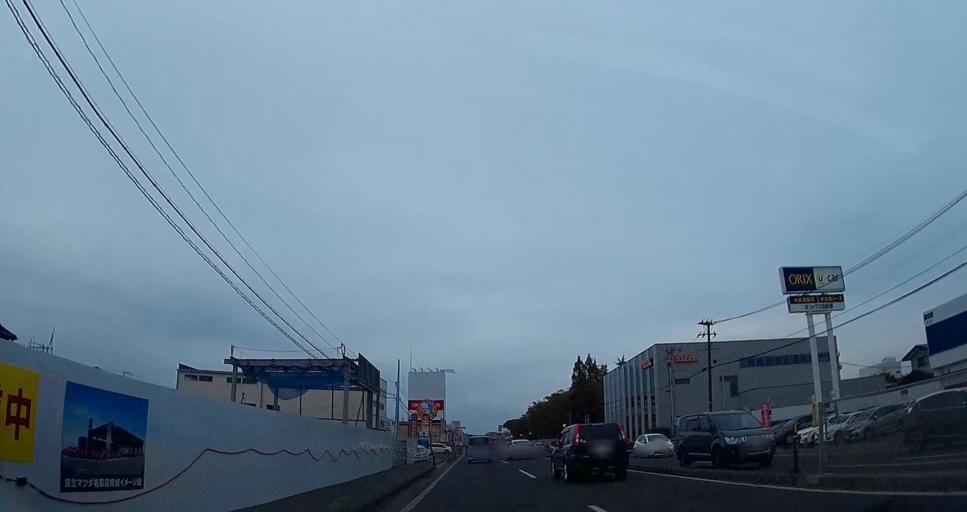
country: JP
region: Miyagi
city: Iwanuma
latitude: 38.1748
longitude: 140.8903
